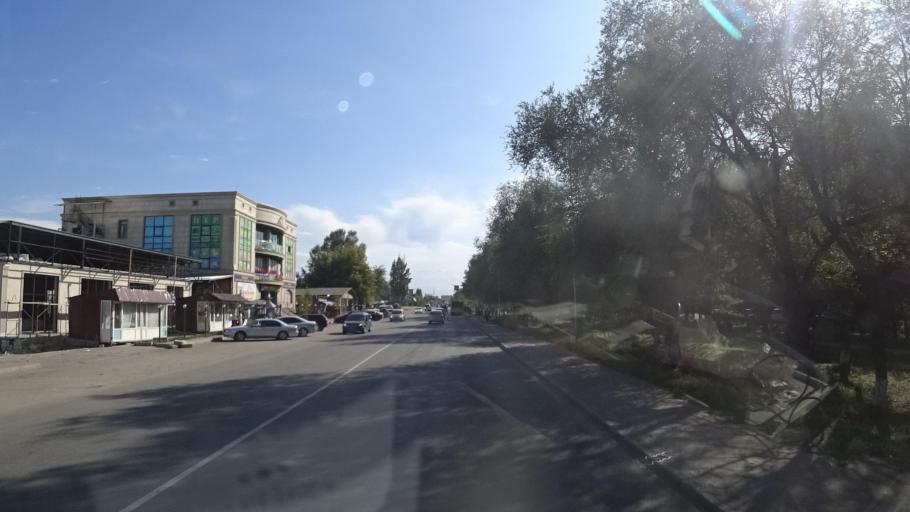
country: KZ
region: Almaty Oblysy
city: Energeticheskiy
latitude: 43.4173
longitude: 77.0212
